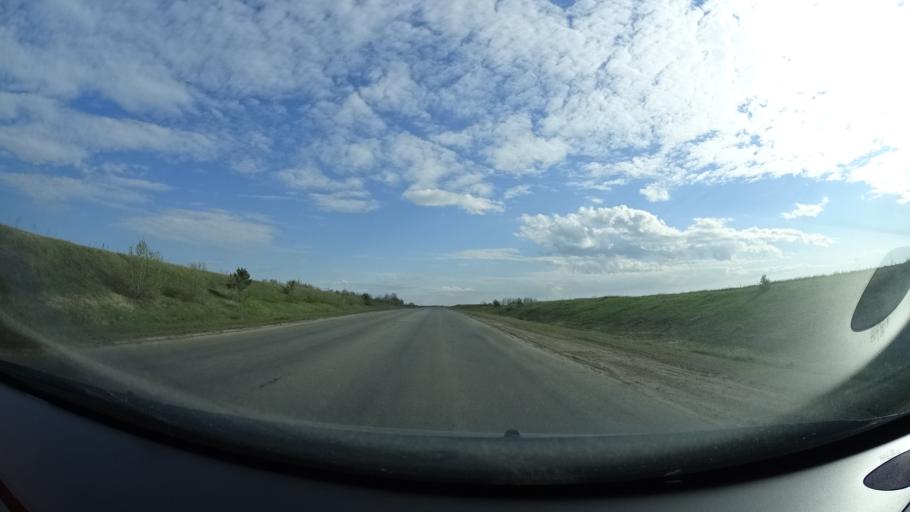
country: RU
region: Bashkortostan
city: Blagoveshchensk
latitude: 55.0898
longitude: 55.8113
